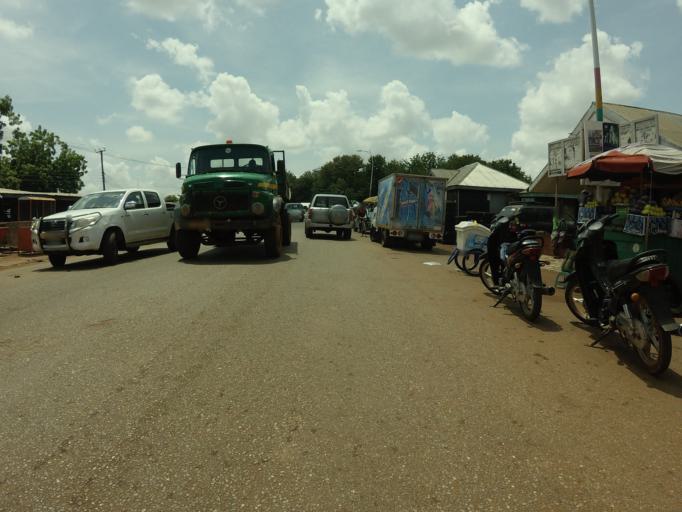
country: GH
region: Northern
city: Tamale
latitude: 9.4048
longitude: -0.8603
